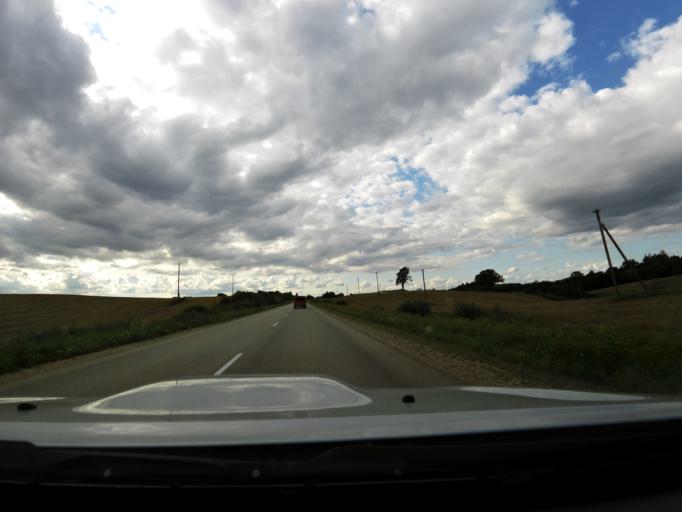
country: LV
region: Ilukste
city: Ilukste
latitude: 55.9738
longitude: 26.0217
